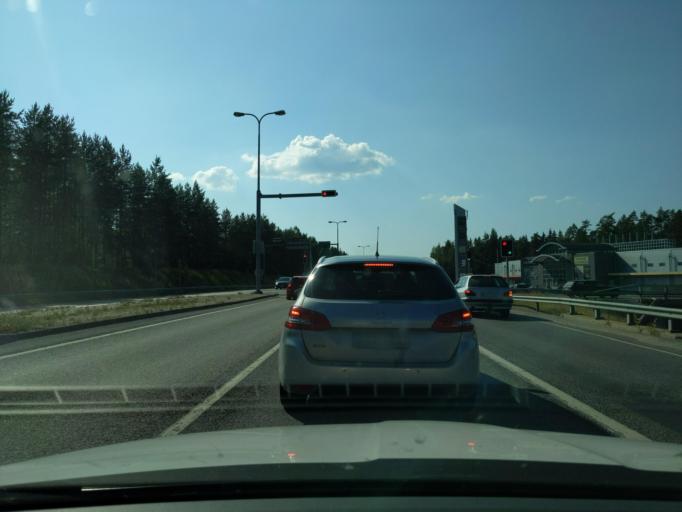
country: FI
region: Paijanne Tavastia
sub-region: Lahti
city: Lahti
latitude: 60.9851
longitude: 25.5801
